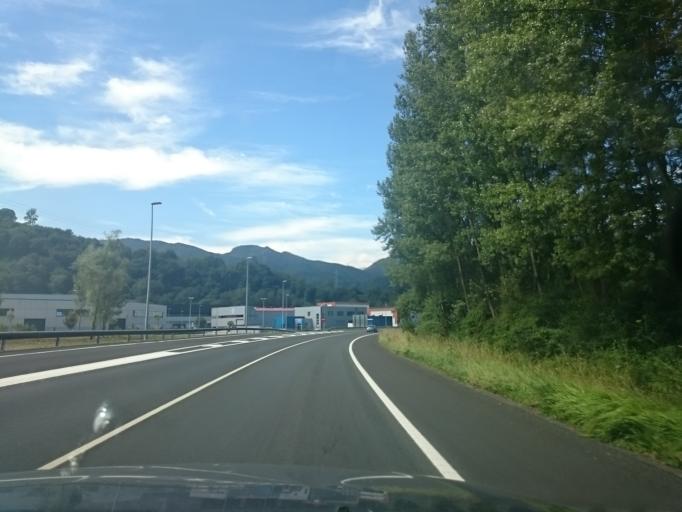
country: ES
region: Asturias
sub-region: Province of Asturias
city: Oviedo
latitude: 43.3091
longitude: -5.8233
